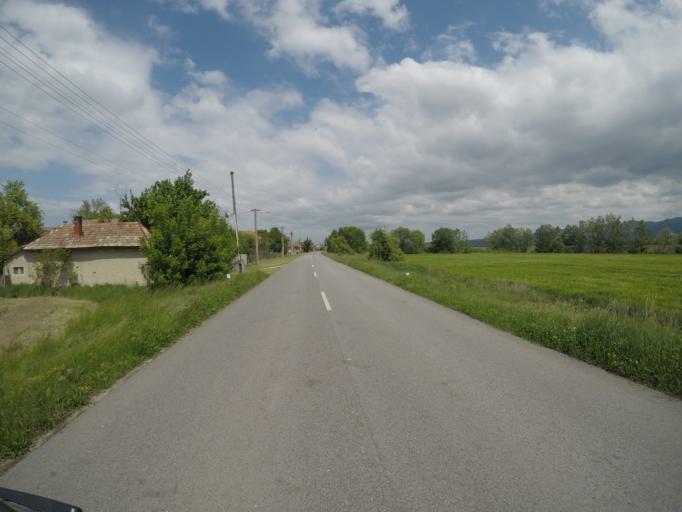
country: SK
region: Nitriansky
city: Zeliezovce
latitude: 47.9891
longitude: 18.7693
